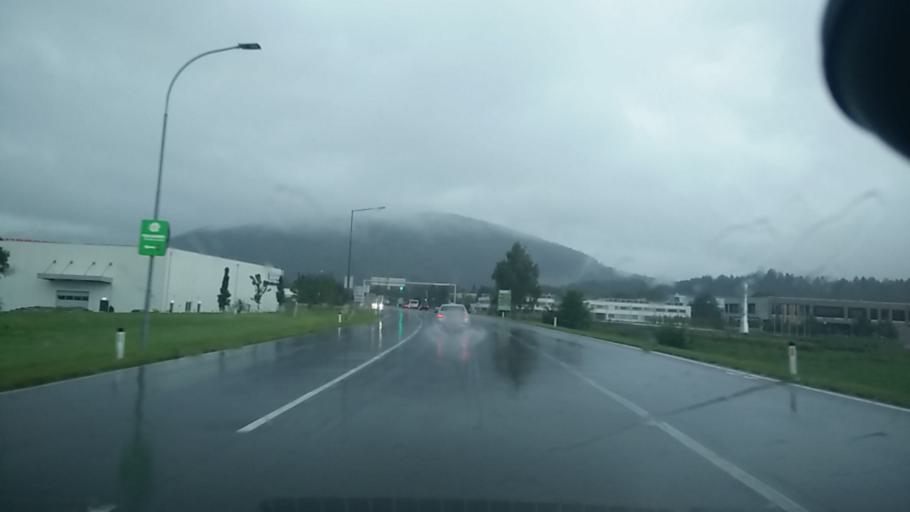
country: AT
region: Carinthia
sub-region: Villach Stadt
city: Villach
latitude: 46.5923
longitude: 13.8349
